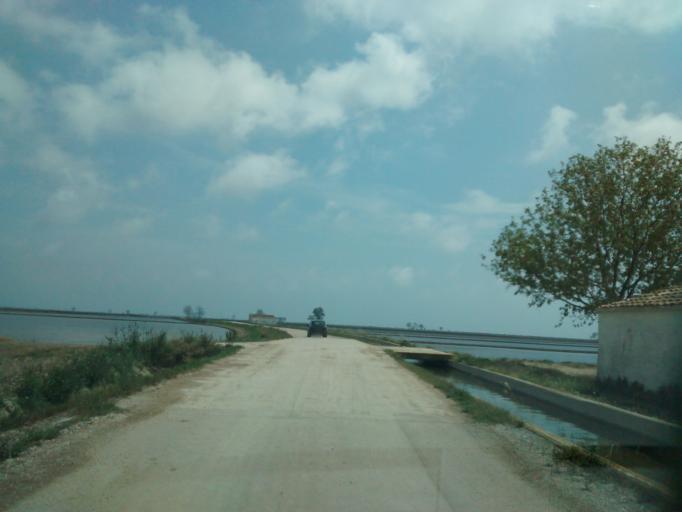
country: ES
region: Catalonia
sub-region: Provincia de Tarragona
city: Deltebre
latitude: 40.6845
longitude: 0.7885
